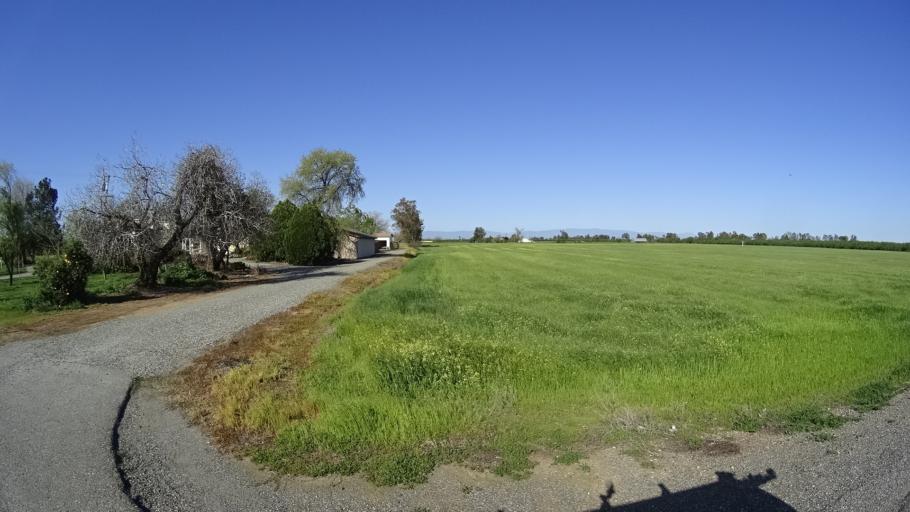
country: US
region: California
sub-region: Glenn County
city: Hamilton City
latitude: 39.7911
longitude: -122.0853
